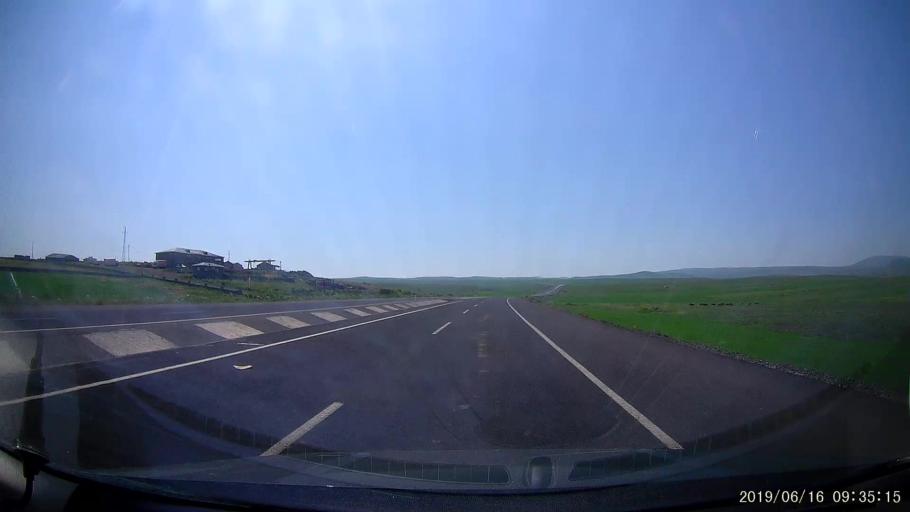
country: TR
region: Kars
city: Kars
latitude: 40.5747
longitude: 43.1526
